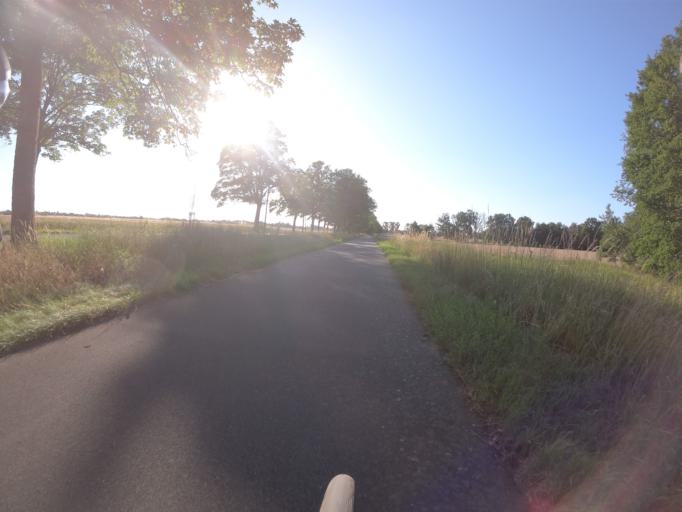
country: DE
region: Brandenburg
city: Niedergorsdorf
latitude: 51.9741
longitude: 13.0000
